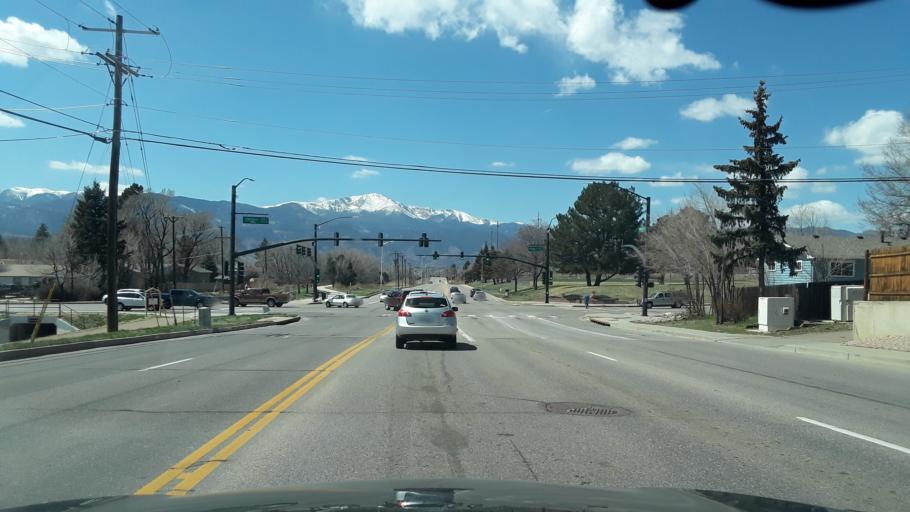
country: US
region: Colorado
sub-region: El Paso County
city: Colorado Springs
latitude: 38.8593
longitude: -104.7748
